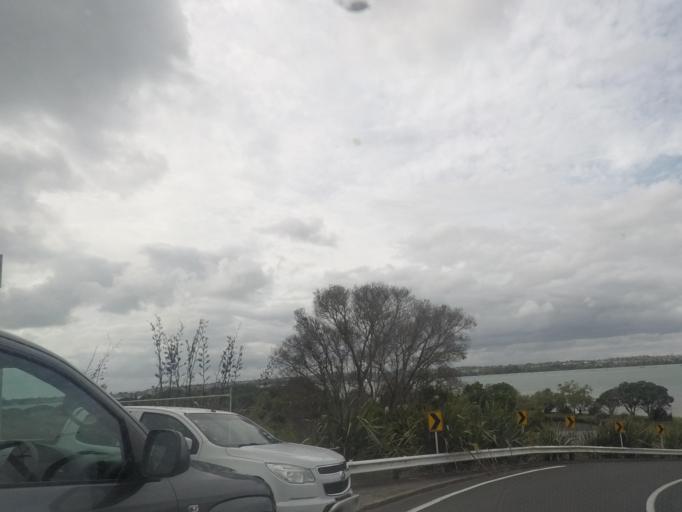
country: NZ
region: Auckland
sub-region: Auckland
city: Tamaki
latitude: -36.8719
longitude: 174.8817
